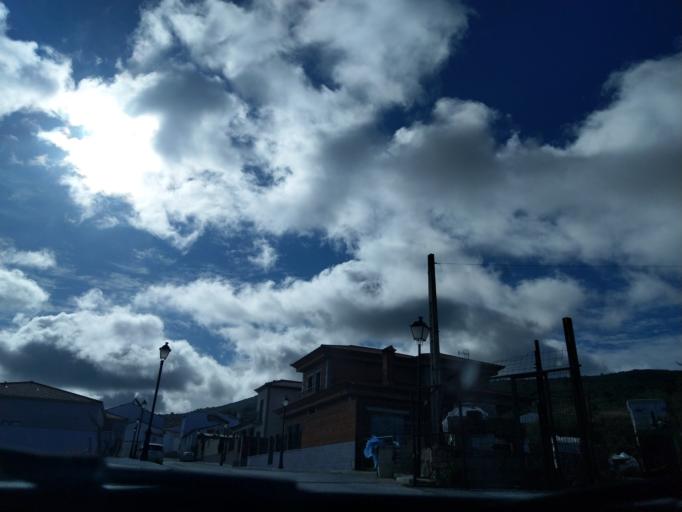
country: ES
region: Extremadura
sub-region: Provincia de Badajoz
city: Reina
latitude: 38.1530
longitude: -5.8987
